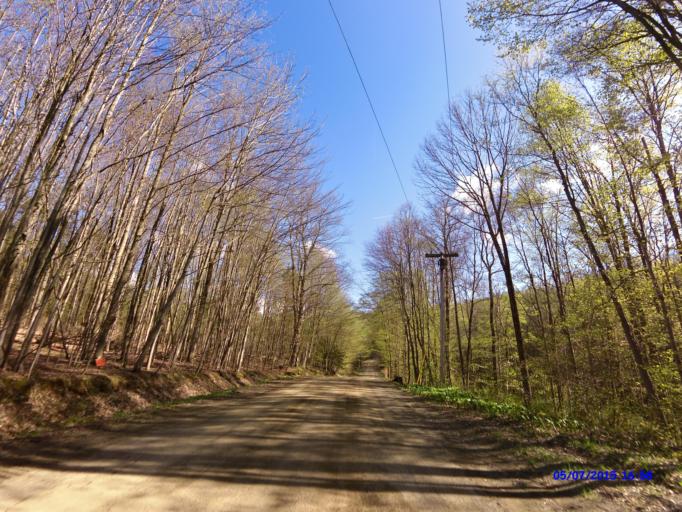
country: US
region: New York
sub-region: Cattaraugus County
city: Little Valley
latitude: 42.2953
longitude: -78.7468
